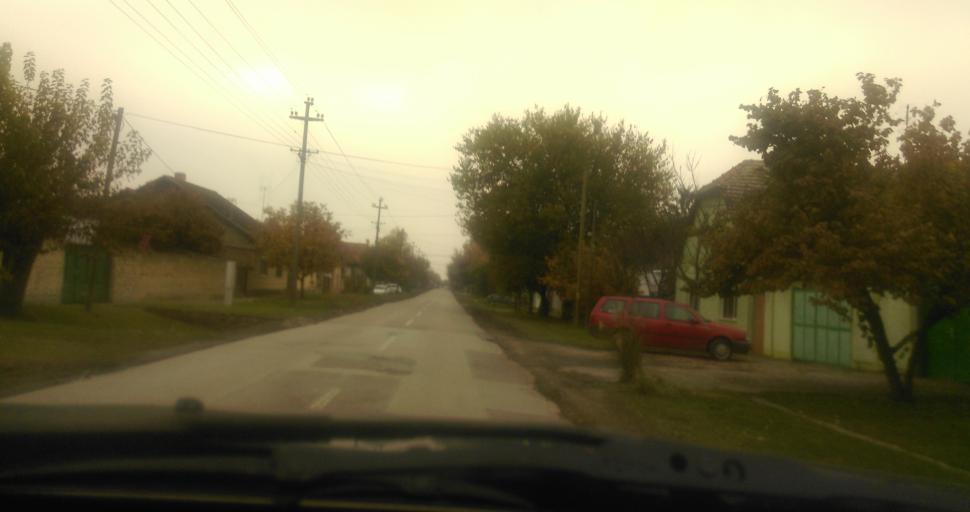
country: RS
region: Autonomna Pokrajina Vojvodina
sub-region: Juznobacki Okrug
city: Becej
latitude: 45.6094
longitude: 20.0311
